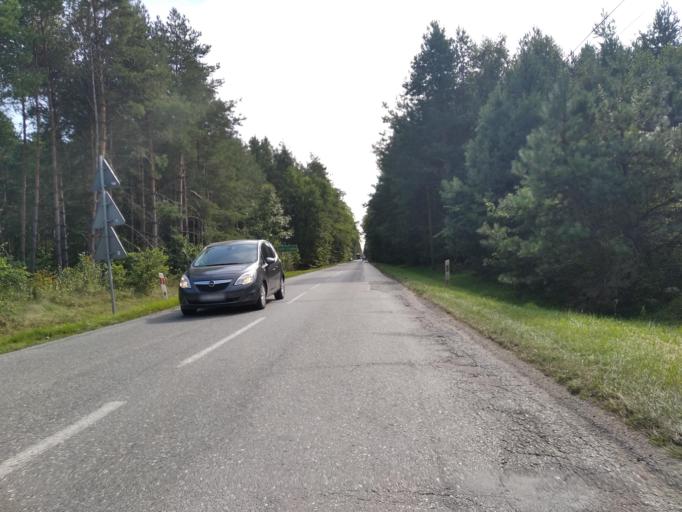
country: PL
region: Subcarpathian Voivodeship
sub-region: Powiat ropczycko-sedziszowski
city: Ostrow
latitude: 50.1518
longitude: 21.5658
